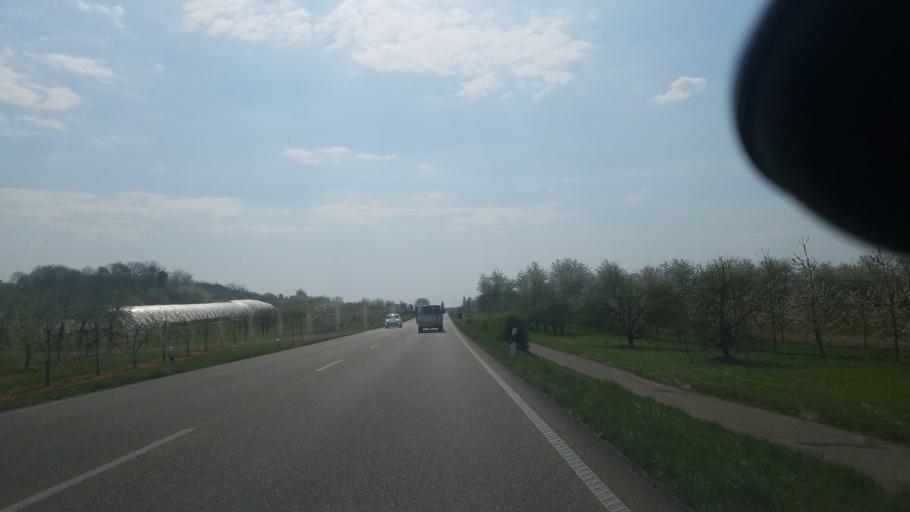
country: DE
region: Baden-Wuerttemberg
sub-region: Freiburg Region
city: Renchen
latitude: 48.6007
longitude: 8.0273
